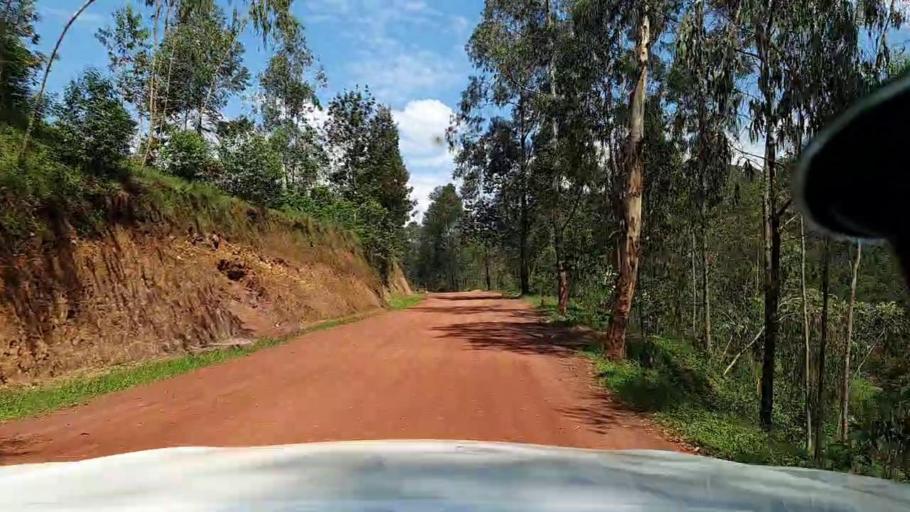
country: RW
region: Kigali
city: Kigali
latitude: -1.7646
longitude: 29.8730
